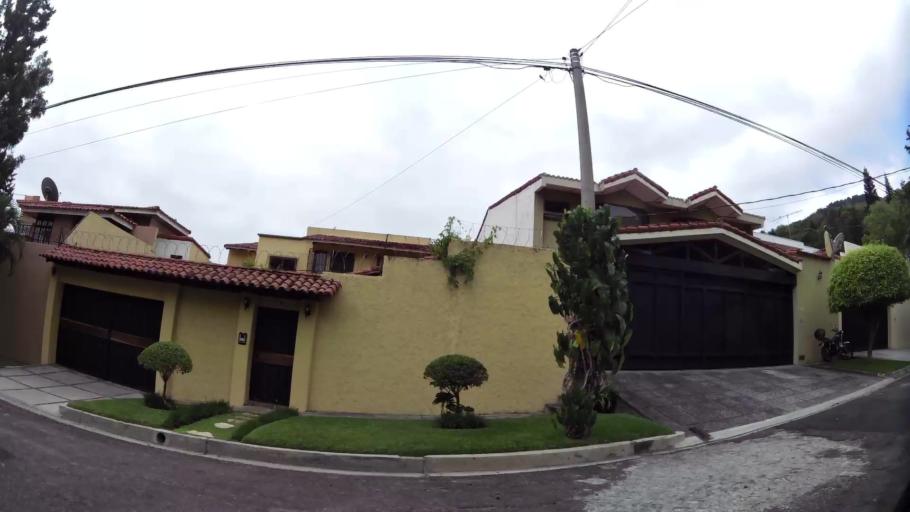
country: SV
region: San Salvador
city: Mejicanos
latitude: 13.7196
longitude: -89.2460
